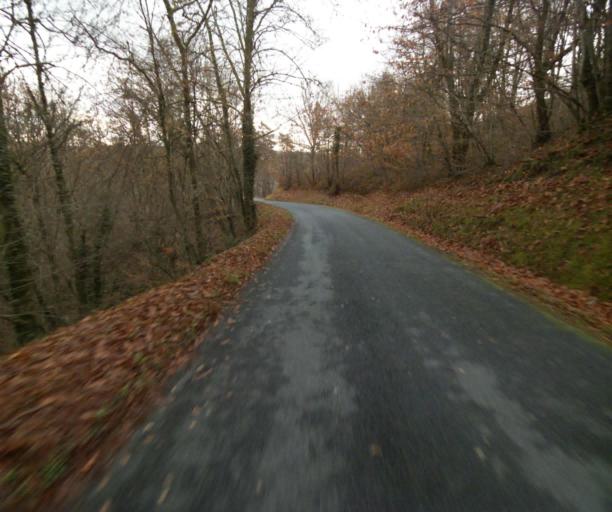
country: FR
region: Limousin
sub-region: Departement de la Correze
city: Chameyrat
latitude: 45.2275
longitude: 1.7031
